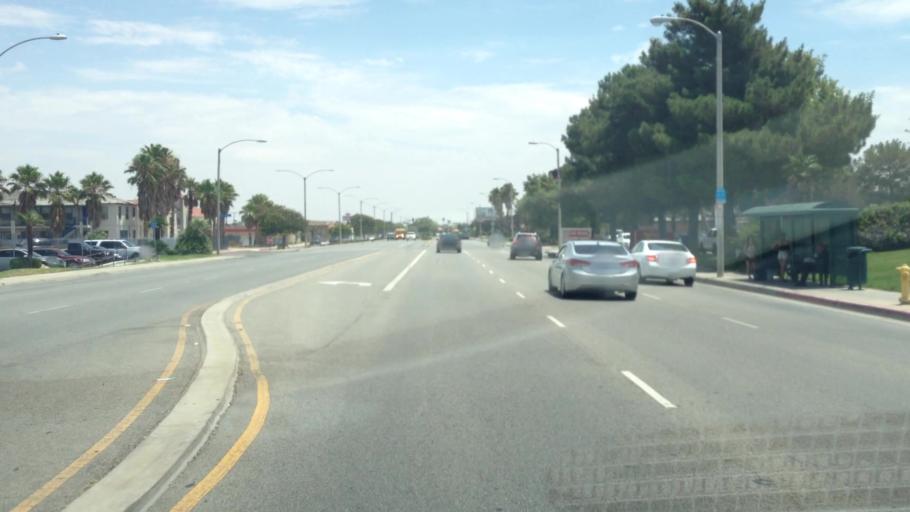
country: US
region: California
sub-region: Los Angeles County
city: Palmdale
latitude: 34.5798
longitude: -118.1287
